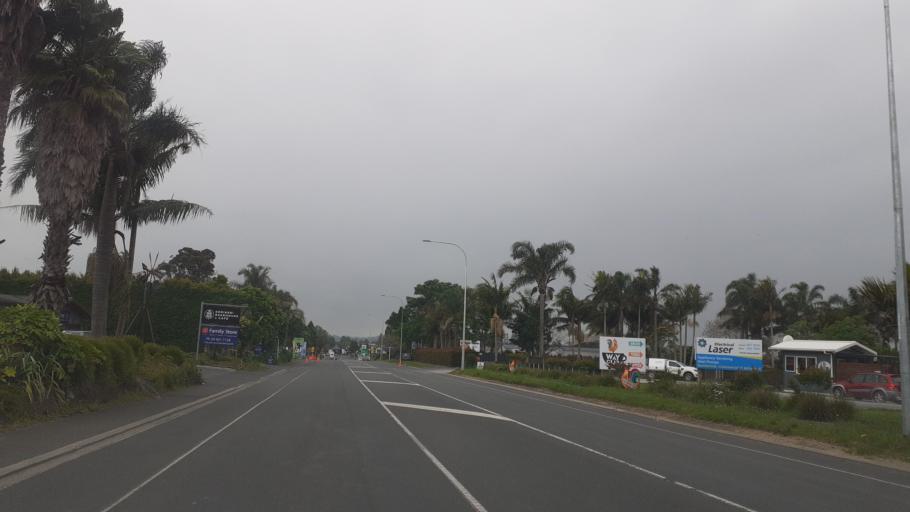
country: NZ
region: Northland
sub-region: Far North District
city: Kerikeri
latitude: -35.2334
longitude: 173.9437
